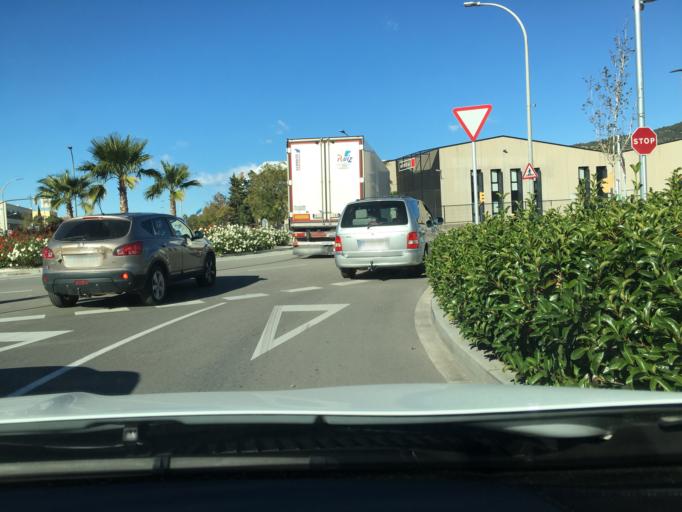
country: ES
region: Catalonia
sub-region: Provincia de Barcelona
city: Sant Feliu de Llobregat
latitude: 41.3874
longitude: 2.0396
